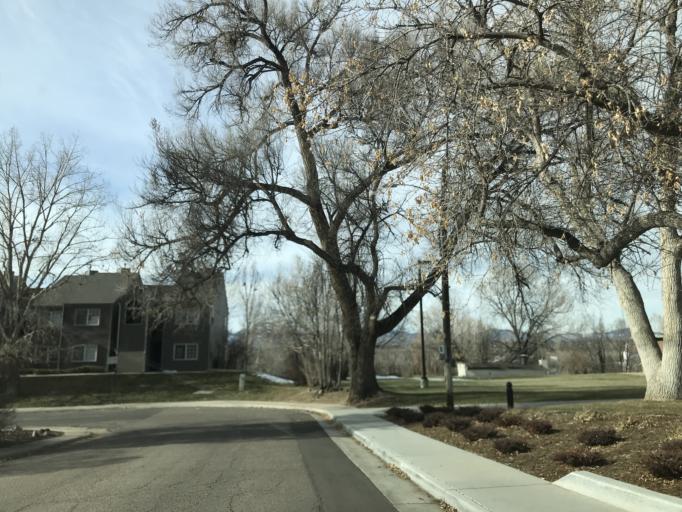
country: US
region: Colorado
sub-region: Arapahoe County
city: Littleton
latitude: 39.6096
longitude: -105.0146
